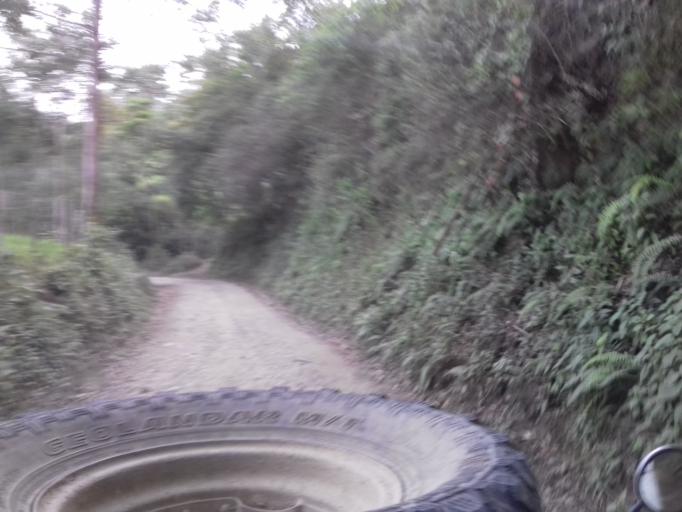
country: CO
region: Quindio
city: Salento
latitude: 4.6202
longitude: -75.5565
